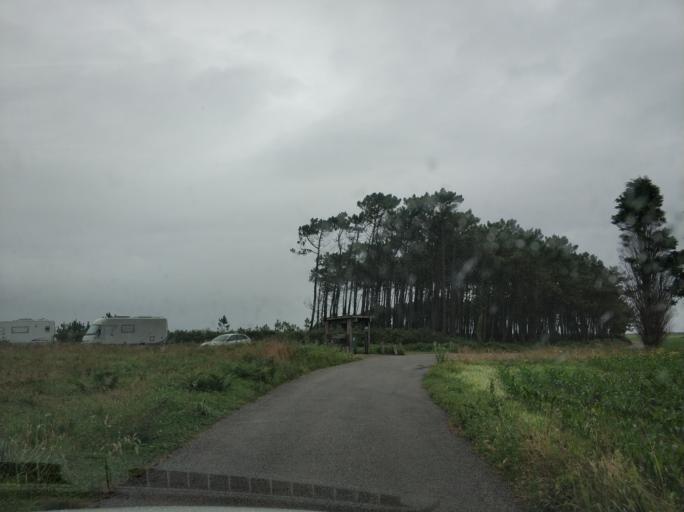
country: ES
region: Asturias
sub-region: Province of Asturias
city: Tineo
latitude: 43.5644
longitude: -6.4701
